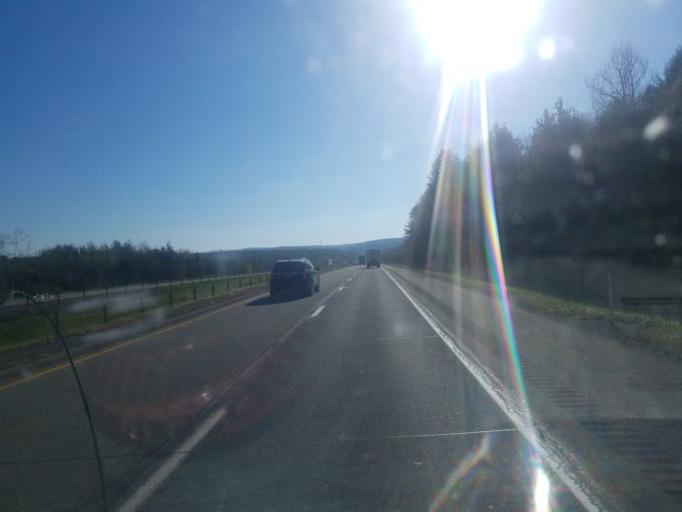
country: US
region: Pennsylvania
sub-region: Cambria County
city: Cresson
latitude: 40.4577
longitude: -78.6232
